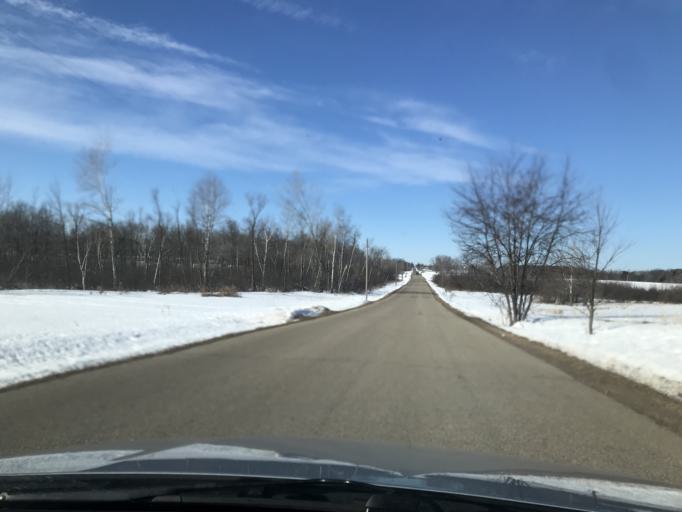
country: US
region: Wisconsin
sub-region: Oconto County
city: Gillett
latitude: 44.9394
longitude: -88.2412
